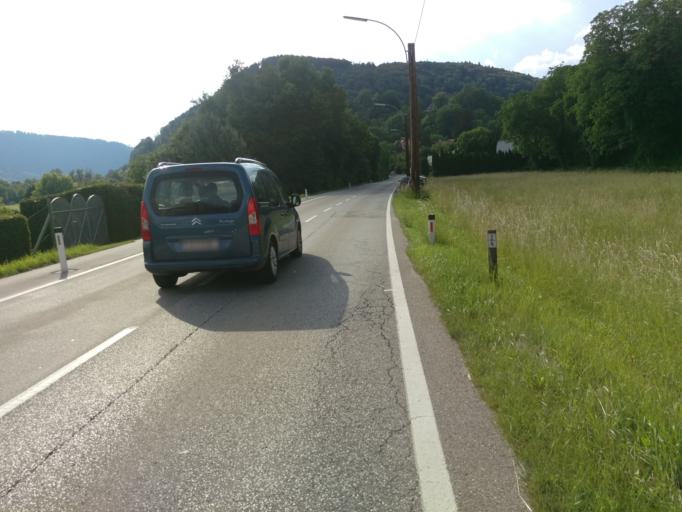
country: AT
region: Styria
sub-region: Graz Stadt
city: Goesting
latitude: 47.1110
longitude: 15.4113
